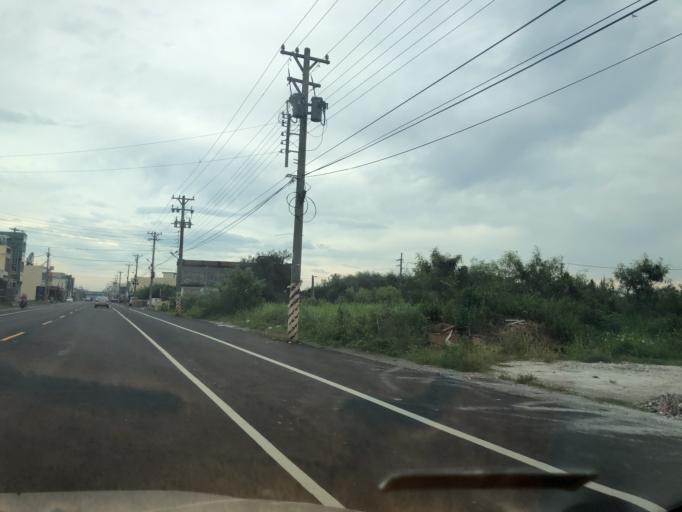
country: TW
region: Taiwan
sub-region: Chiayi
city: Taibao
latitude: 23.7063
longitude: 120.2006
